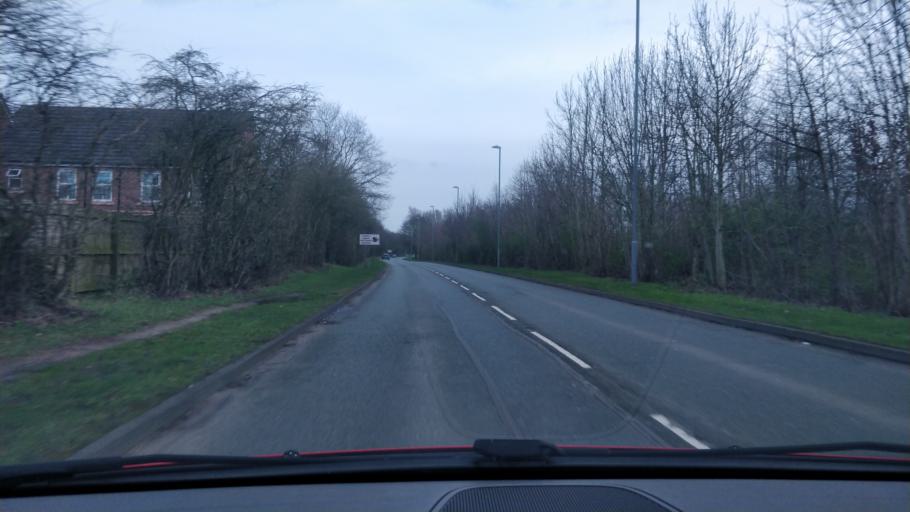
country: GB
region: England
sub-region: Knowsley
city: Huyton
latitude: 53.4283
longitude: -2.8544
